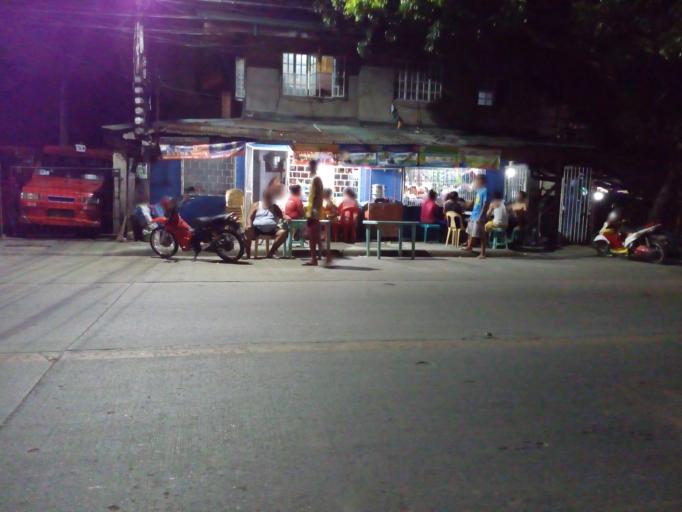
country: PH
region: Central Visayas
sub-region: Cebu City
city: Calero
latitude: 10.3021
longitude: 123.8780
